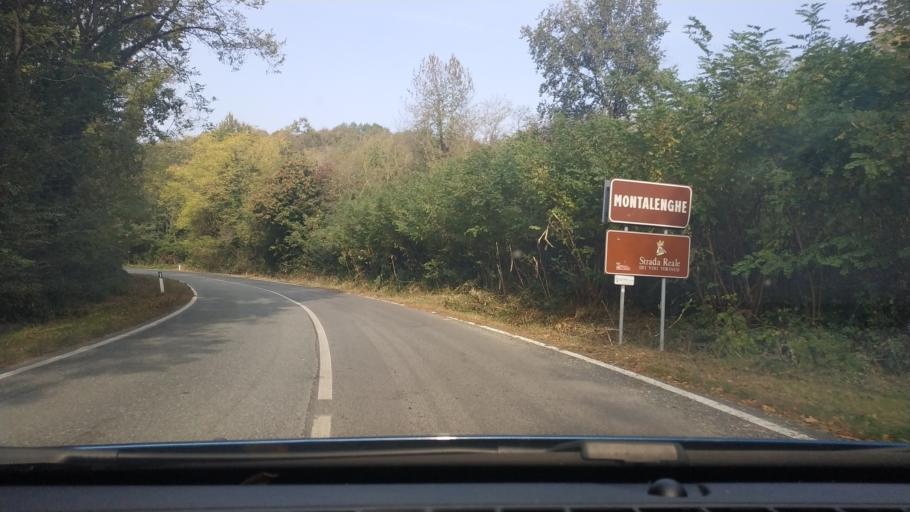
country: IT
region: Piedmont
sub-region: Provincia di Torino
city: Montalenghe
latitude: 45.3364
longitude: 7.8484
